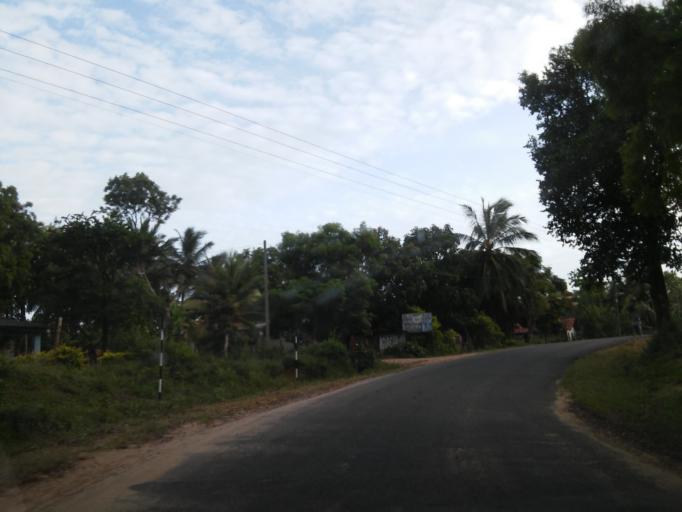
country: LK
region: Central
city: Sigiriya
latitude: 8.1177
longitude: 80.6324
